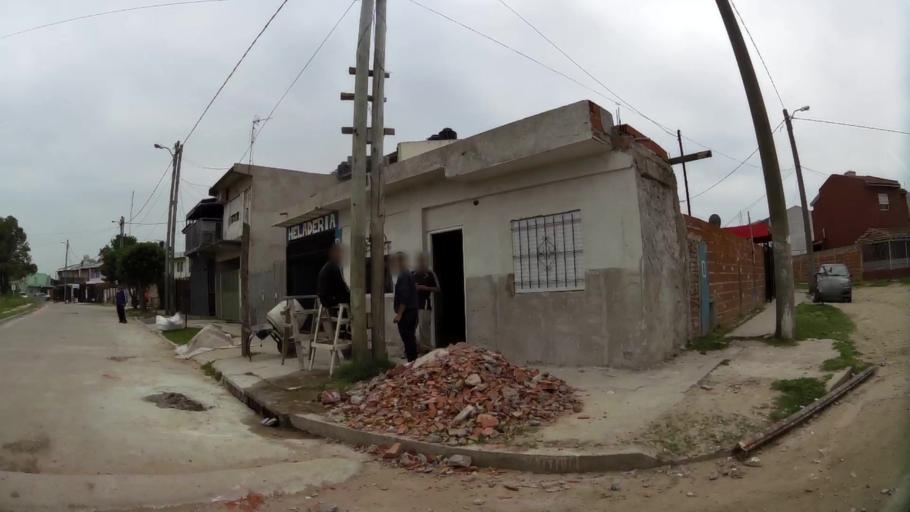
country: AR
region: Buenos Aires
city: San Justo
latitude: -34.6995
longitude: -58.5474
